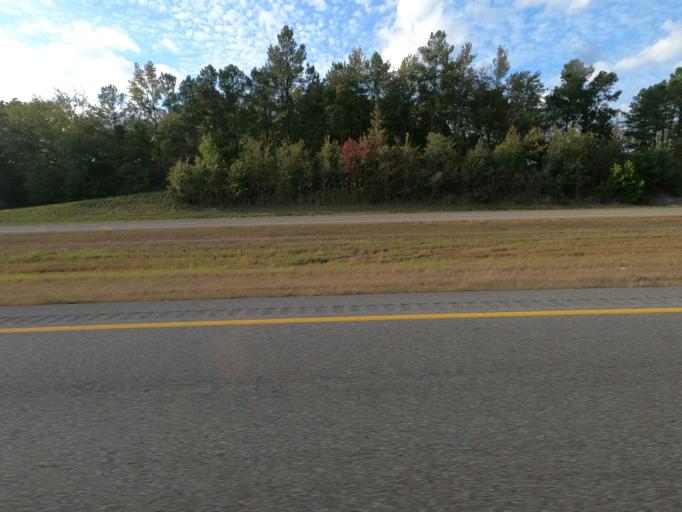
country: US
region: Tennessee
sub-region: Humphreys County
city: New Johnsonville
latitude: 35.8515
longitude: -88.0654
